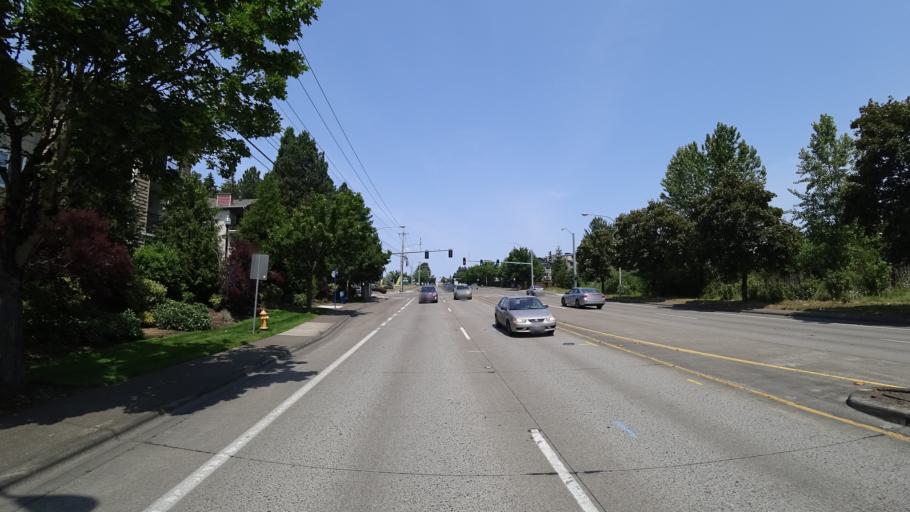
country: US
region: Oregon
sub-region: Washington County
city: Aloha
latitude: 45.5229
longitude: -122.8676
